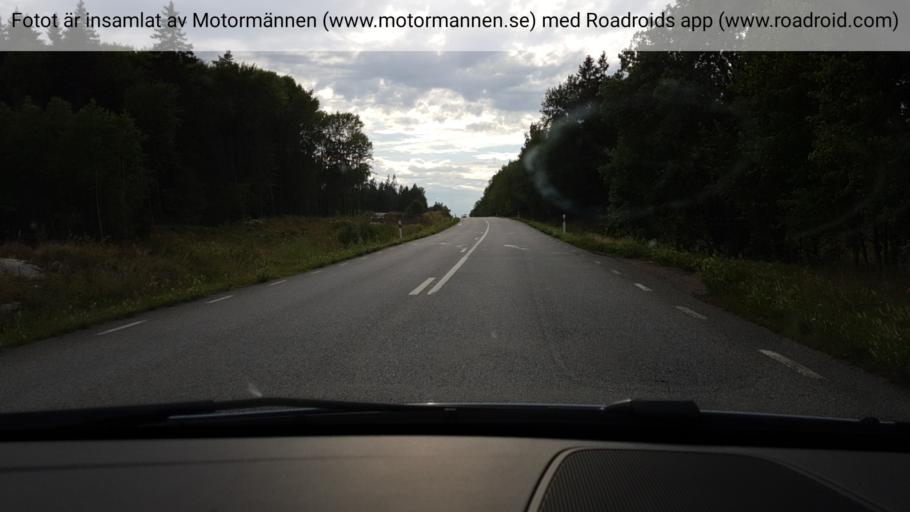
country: SE
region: Uppsala
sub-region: Knivsta Kommun
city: Knivsta
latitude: 59.8545
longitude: 17.8876
